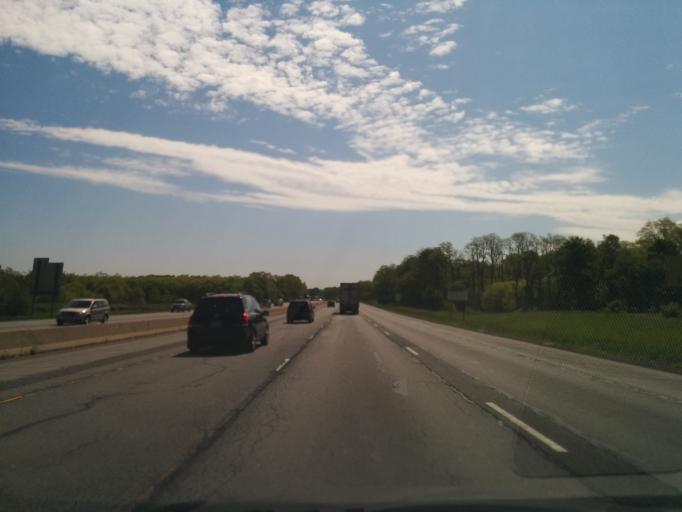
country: US
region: Indiana
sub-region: Porter County
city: Portage
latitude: 41.6017
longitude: -87.1592
